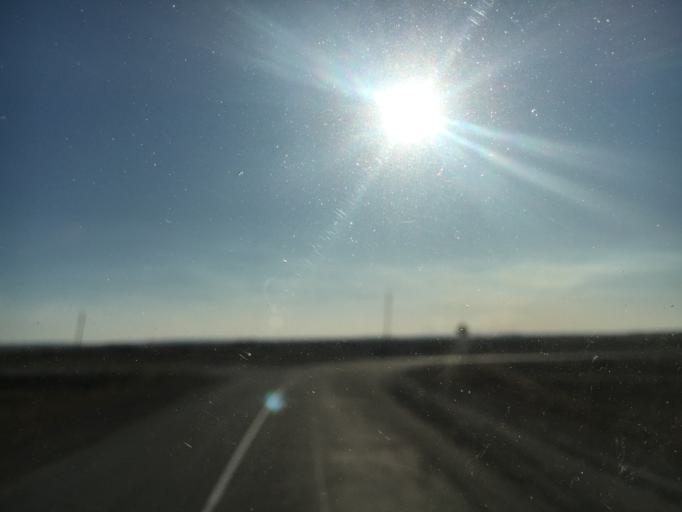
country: KZ
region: Qaraghandy
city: Tokarevka
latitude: 50.1203
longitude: 73.2119
